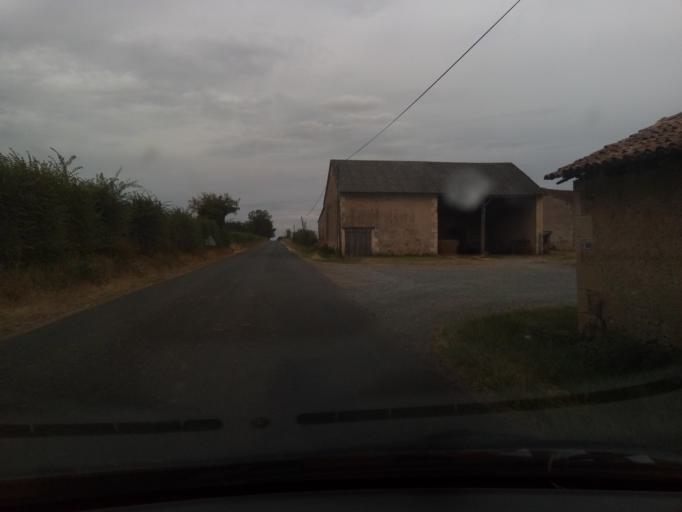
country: FR
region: Poitou-Charentes
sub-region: Departement de la Vienne
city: Pleumartin
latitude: 46.6331
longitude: 0.7569
